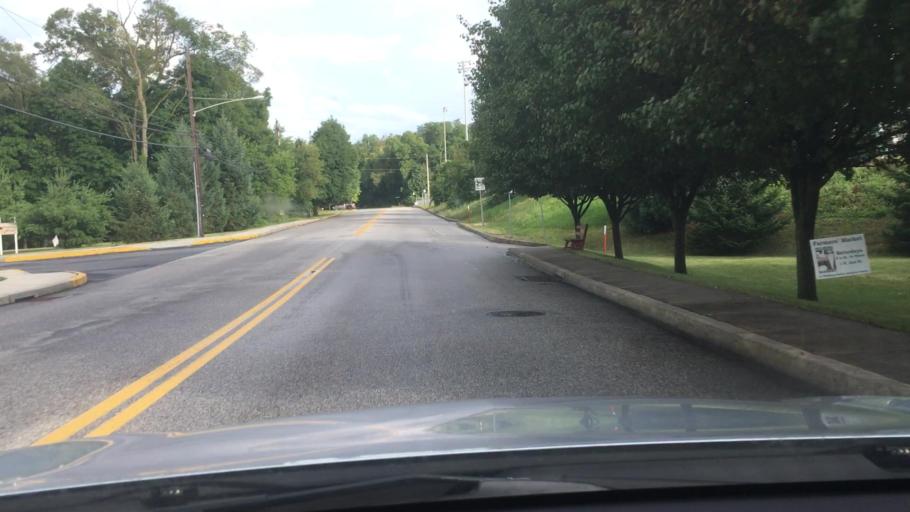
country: US
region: Pennsylvania
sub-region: York County
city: Dillsburg
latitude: 40.1094
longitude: -77.0330
